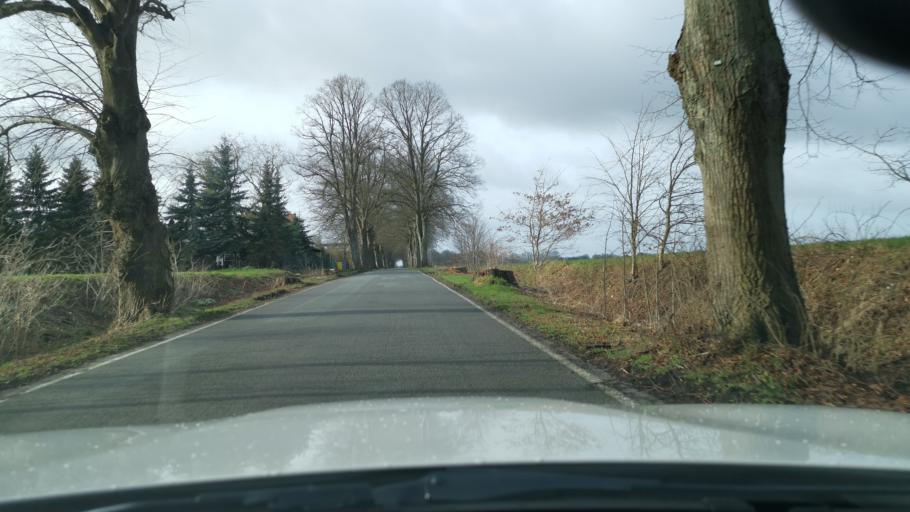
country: DE
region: Mecklenburg-Vorpommern
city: Wardow
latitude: 53.9983
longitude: 12.3814
